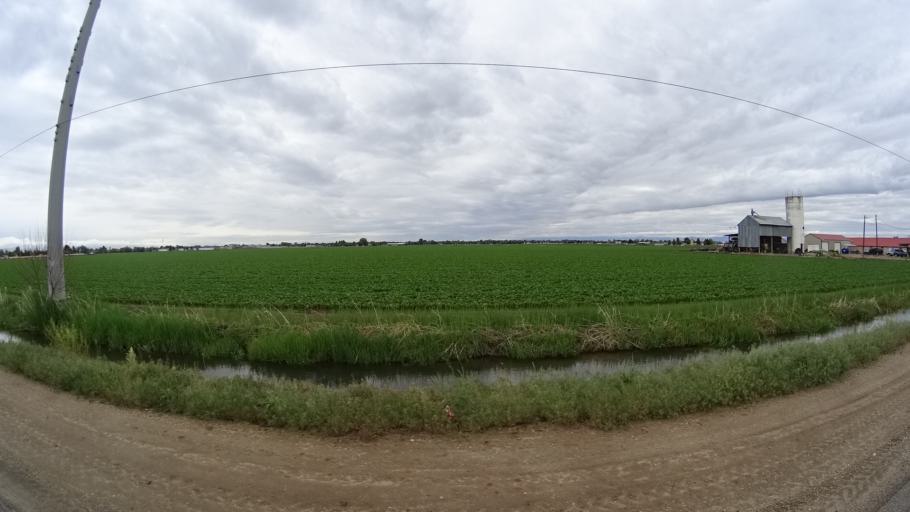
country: US
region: Idaho
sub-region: Ada County
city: Star
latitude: 43.6487
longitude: -116.4470
